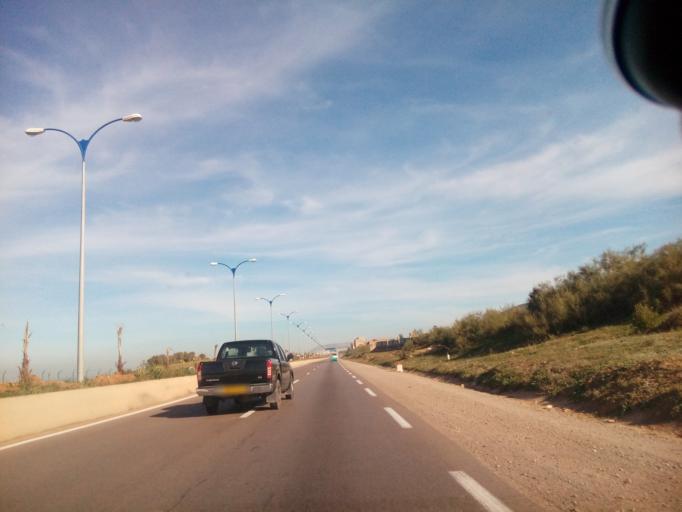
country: DZ
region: Mostaganem
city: Mostaganem
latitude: 35.8611
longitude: 0.0323
